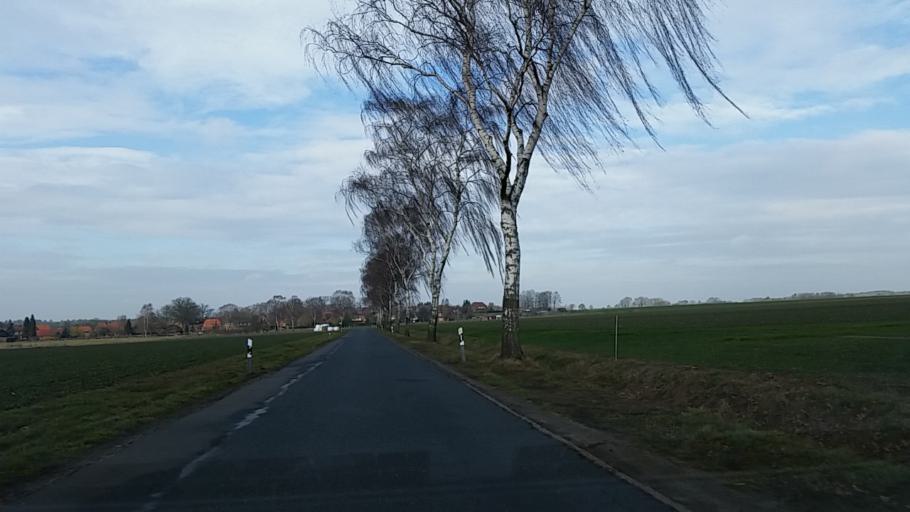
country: DE
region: Lower Saxony
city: Altenmedingen
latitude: 53.1441
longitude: 10.6252
